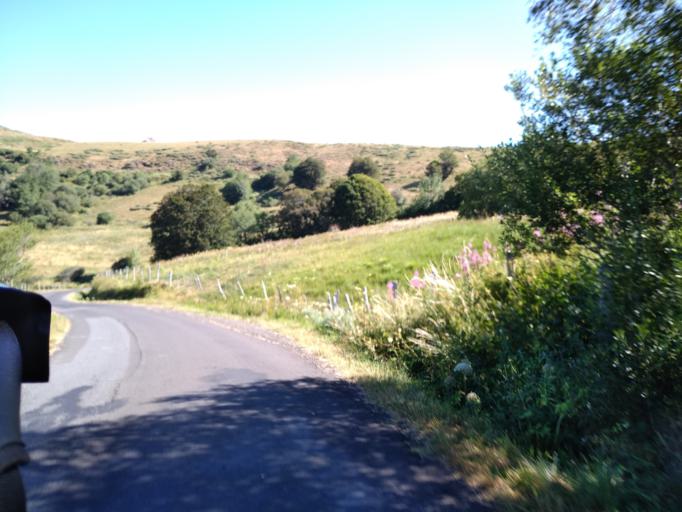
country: FR
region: Auvergne
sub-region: Departement du Cantal
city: Pierrefort
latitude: 45.0125
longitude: 2.8133
